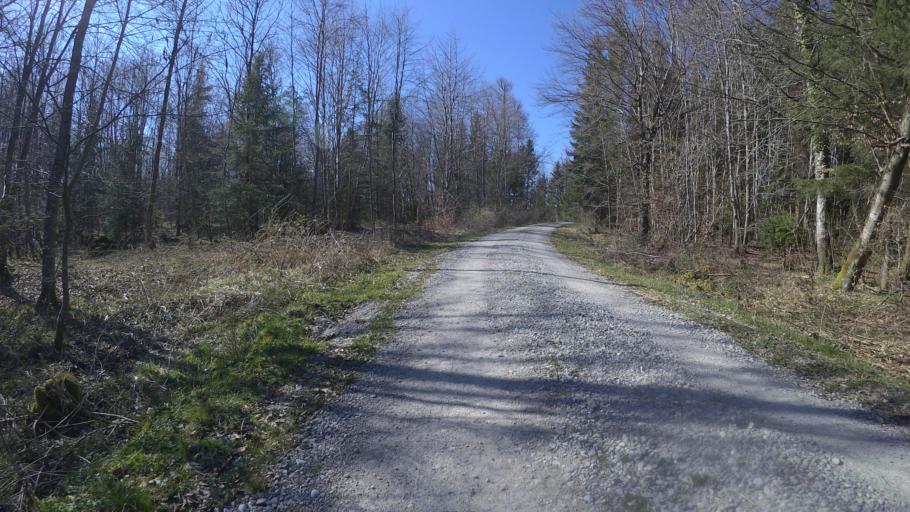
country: DE
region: Bavaria
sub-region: Upper Bavaria
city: Seeon-Seebruck
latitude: 47.9614
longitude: 12.4857
